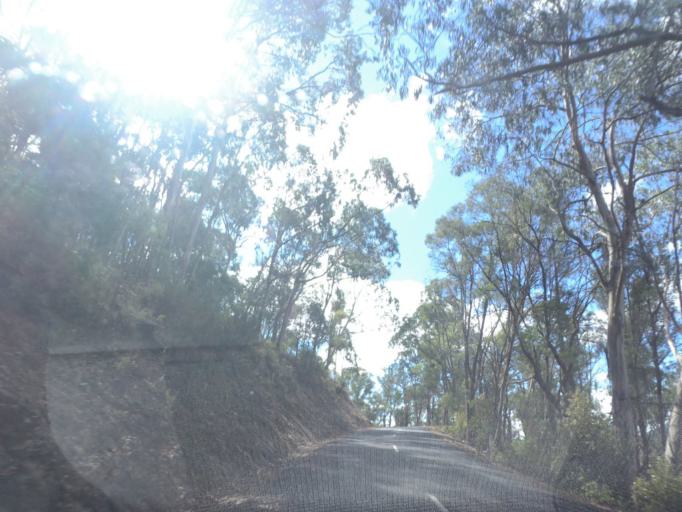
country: AU
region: Victoria
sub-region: Murrindindi
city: Alexandra
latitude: -37.3366
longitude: 145.9547
